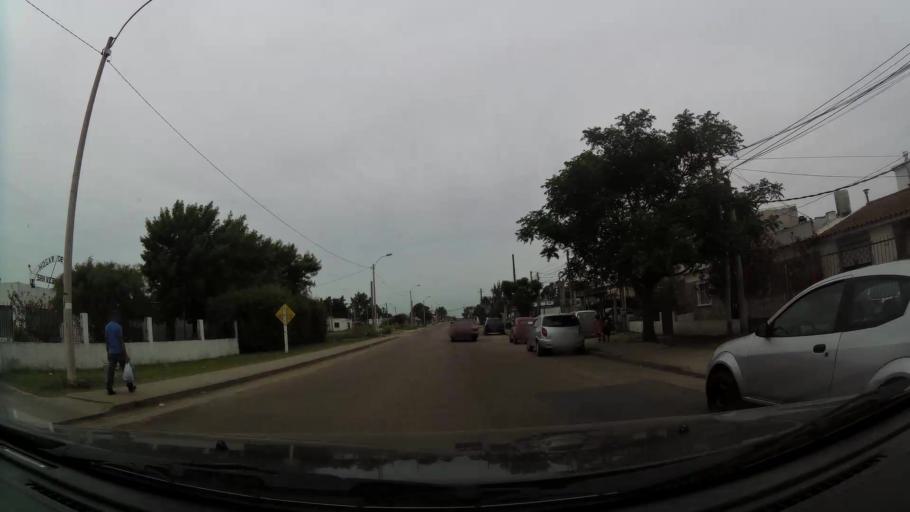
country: UY
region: Canelones
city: Las Piedras
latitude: -34.7353
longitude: -56.2166
